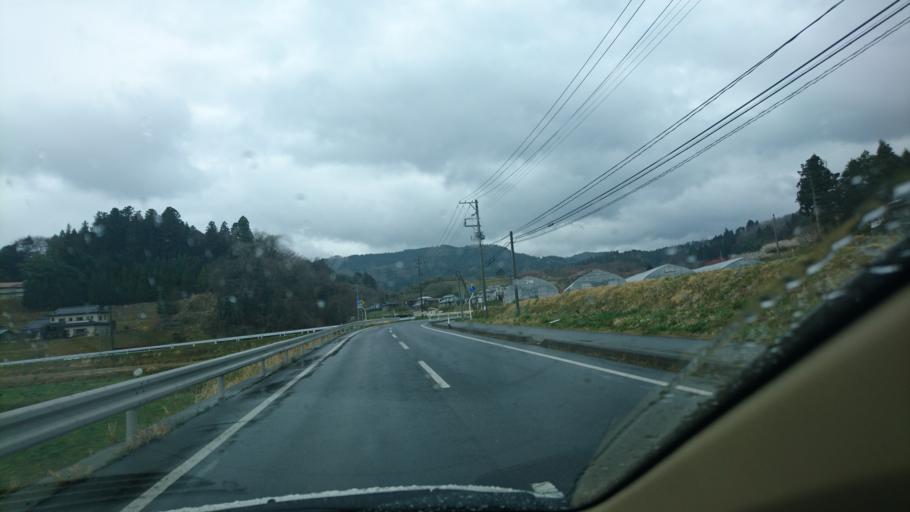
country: JP
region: Iwate
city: Ichinoseki
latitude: 38.9267
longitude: 141.3178
